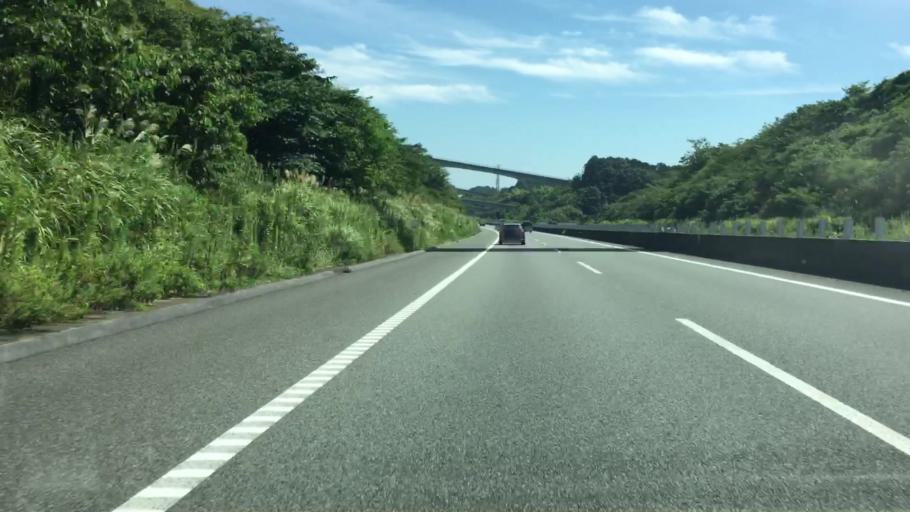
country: JP
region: Shizuoka
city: Fuji
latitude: 35.1684
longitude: 138.7512
